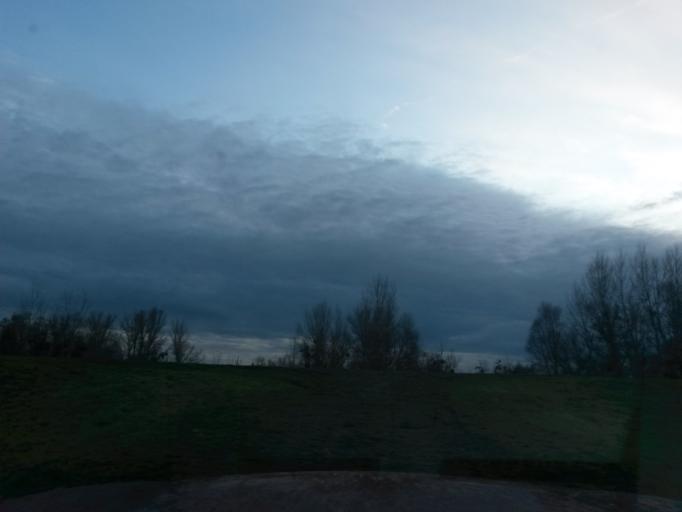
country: HU
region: Borsod-Abauj-Zemplen
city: Ricse
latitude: 48.4915
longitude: 21.9217
